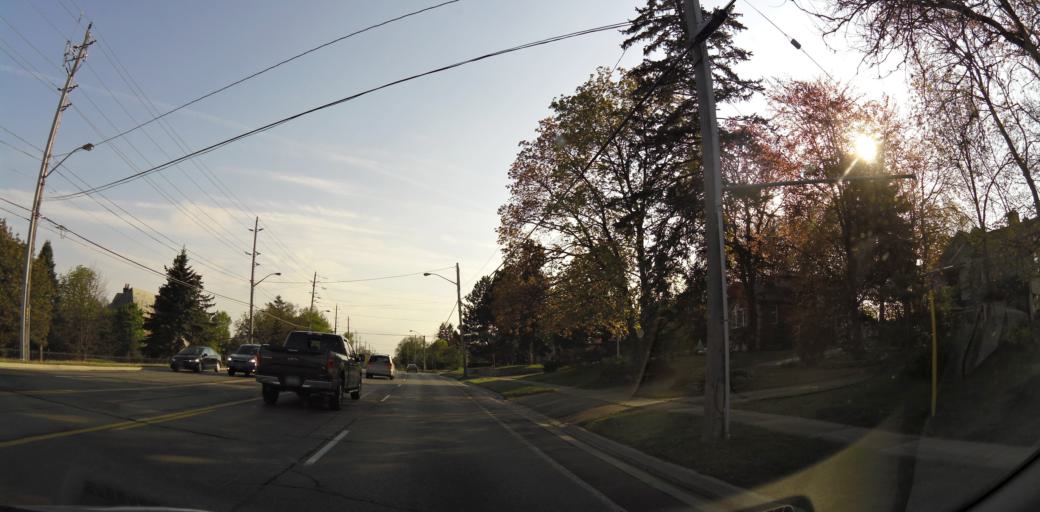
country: CA
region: Ontario
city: Hamilton
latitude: 43.2989
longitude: -79.8631
